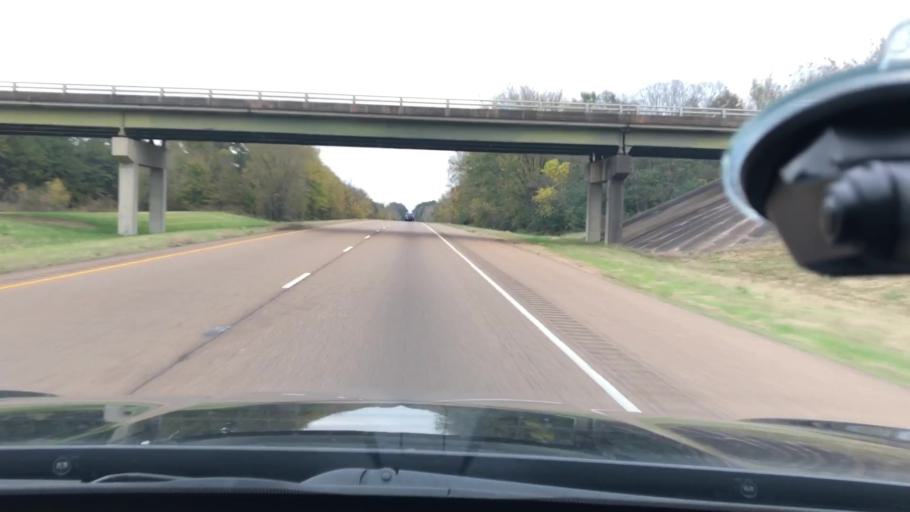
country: US
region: Arkansas
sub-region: Nevada County
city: Prescott
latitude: 33.7660
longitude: -93.4839
